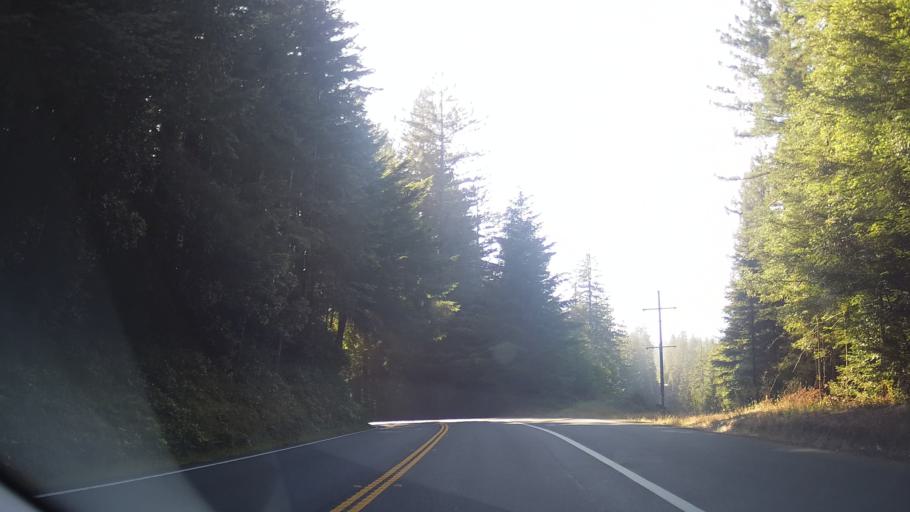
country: US
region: California
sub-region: Mendocino County
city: Fort Bragg
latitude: 39.3768
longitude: -123.6865
